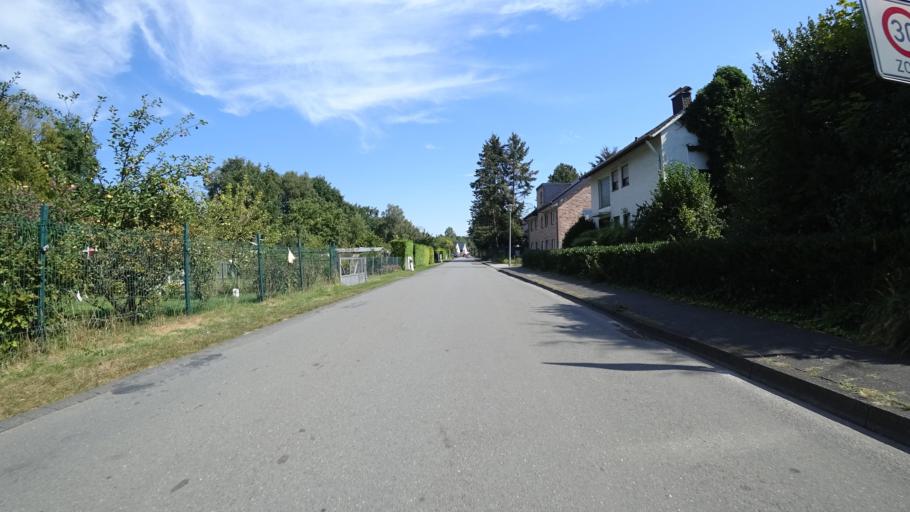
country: DE
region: North Rhine-Westphalia
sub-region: Regierungsbezirk Detmold
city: Guetersloh
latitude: 51.9401
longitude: 8.4398
